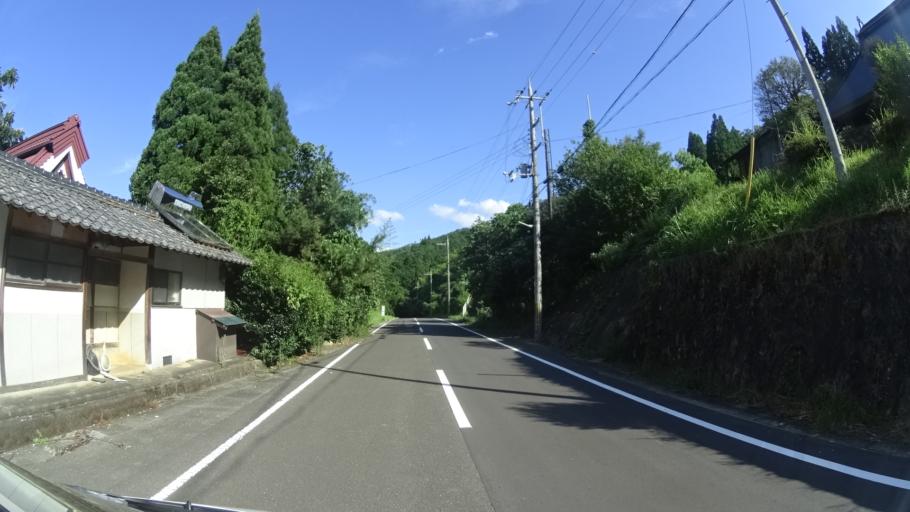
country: JP
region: Kyoto
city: Ayabe
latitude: 35.2758
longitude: 135.3323
